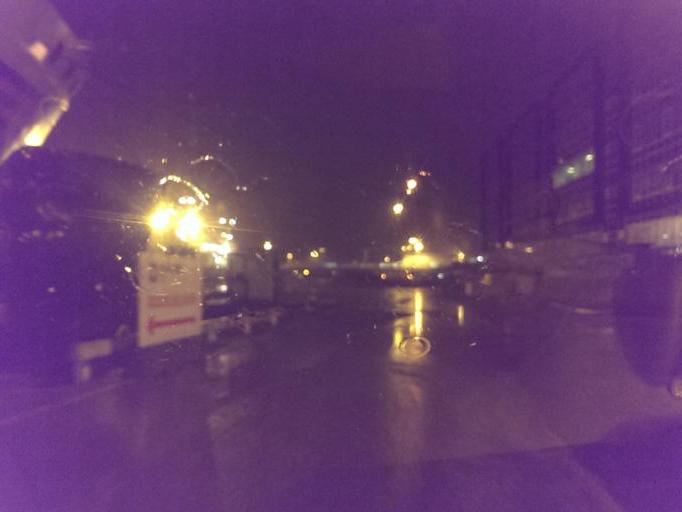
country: DK
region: South Denmark
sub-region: Esbjerg Kommune
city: Esbjerg
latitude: 55.4607
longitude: 8.4467
